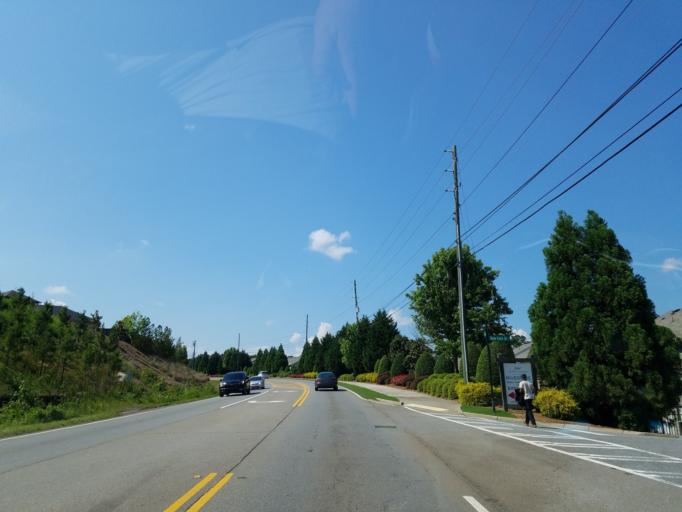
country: US
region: Georgia
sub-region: Cherokee County
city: Woodstock
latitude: 34.1332
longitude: -84.4978
